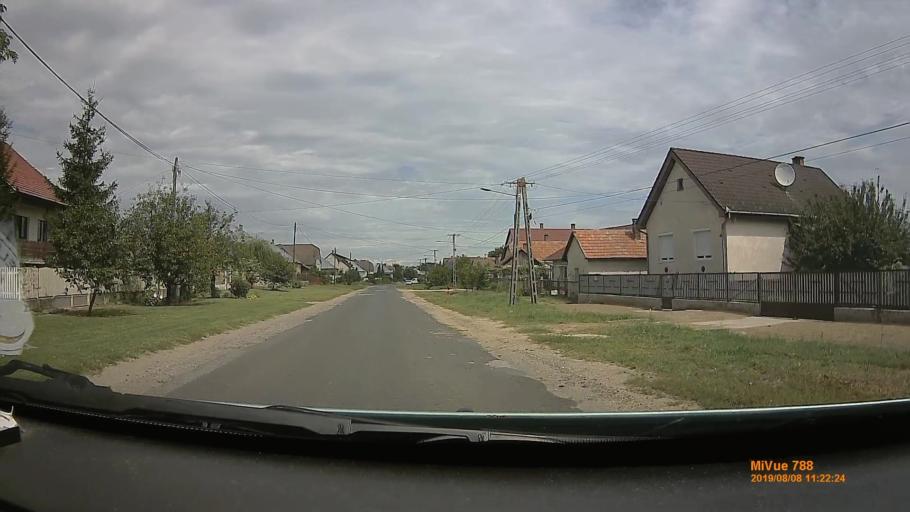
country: HU
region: Szabolcs-Szatmar-Bereg
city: Balkany
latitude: 47.7611
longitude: 21.8482
